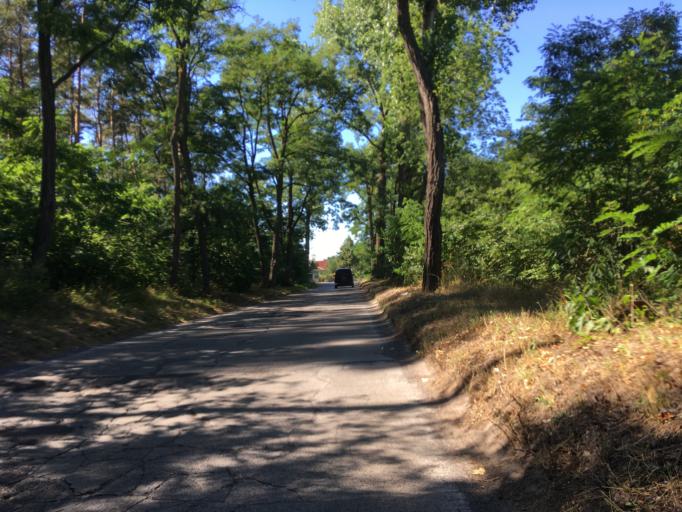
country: DE
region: Brandenburg
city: Schulzendorf
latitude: 52.3556
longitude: 13.5894
